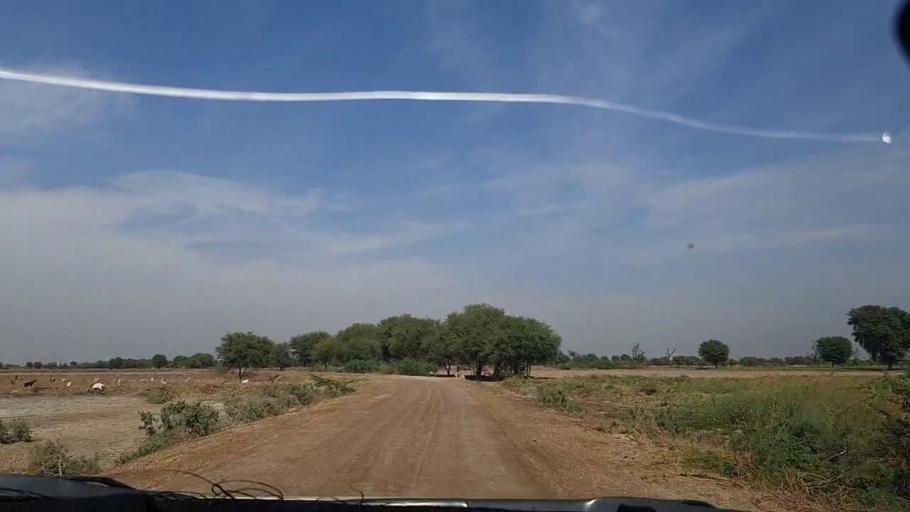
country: PK
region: Sindh
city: Pithoro
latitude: 25.4987
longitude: 69.4587
